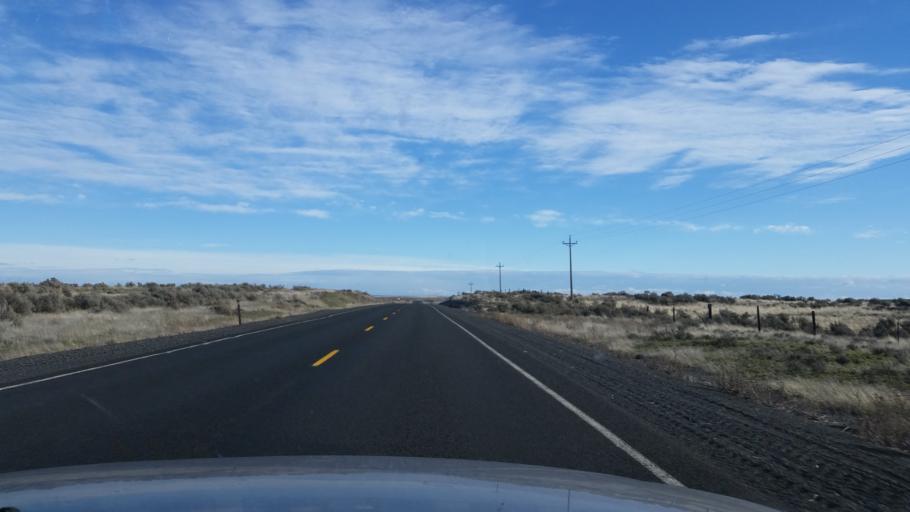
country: US
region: Washington
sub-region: Grant County
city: Warden
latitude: 47.3145
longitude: -118.7940
